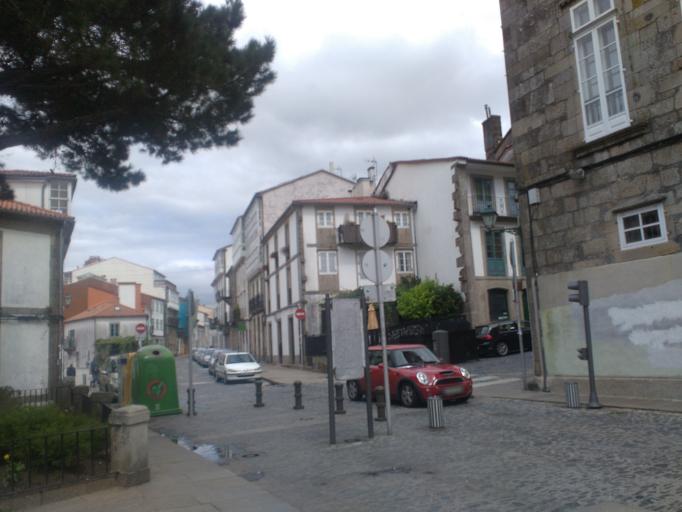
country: ES
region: Galicia
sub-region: Provincia da Coruna
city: Santiago de Compostela
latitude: 42.8833
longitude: -8.5432
